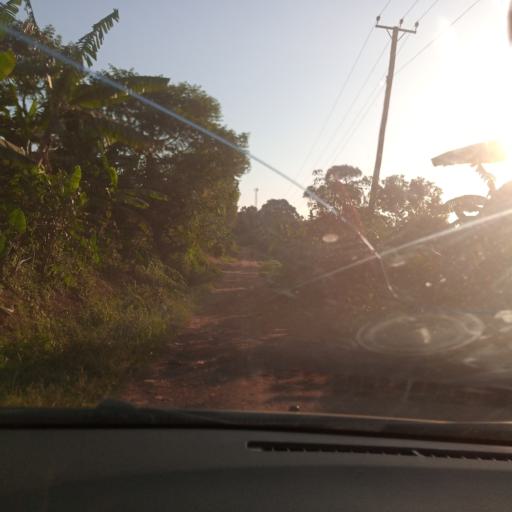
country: UG
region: Central Region
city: Masaka
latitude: -0.3418
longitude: 31.7604
